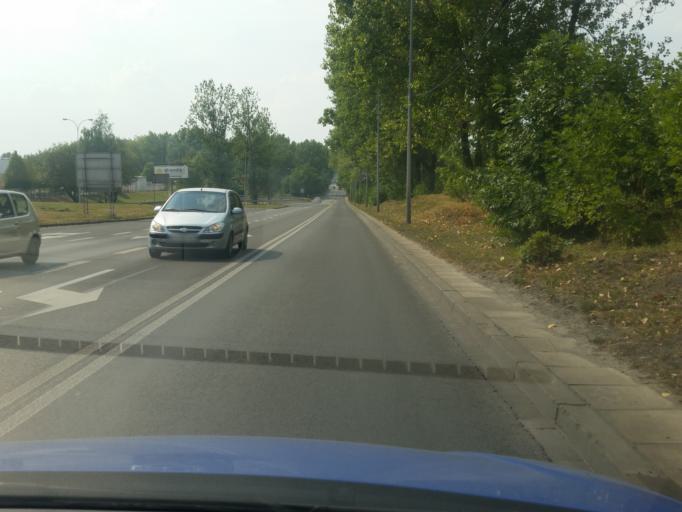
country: PL
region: Silesian Voivodeship
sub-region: Sosnowiec
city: Sosnowiec
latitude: 50.2493
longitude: 19.1167
